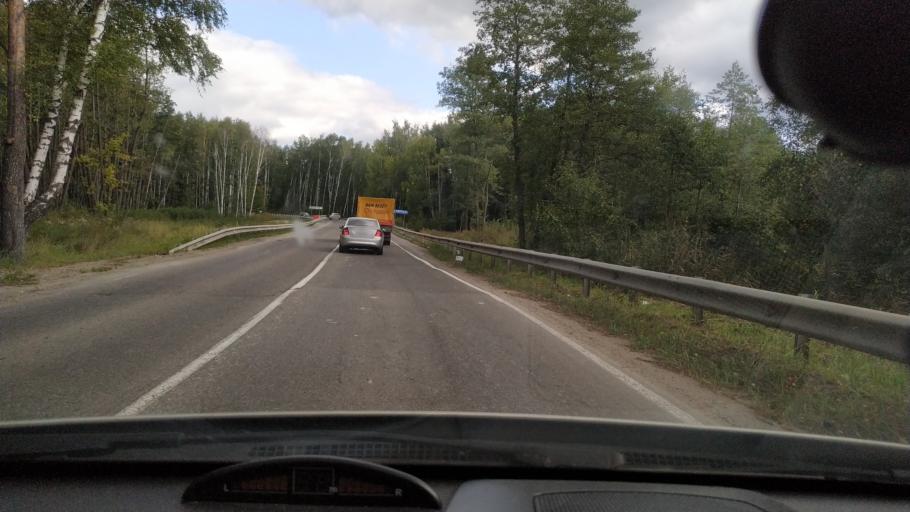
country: RU
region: Moskovskaya
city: Chornaya
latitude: 55.7665
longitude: 38.0585
